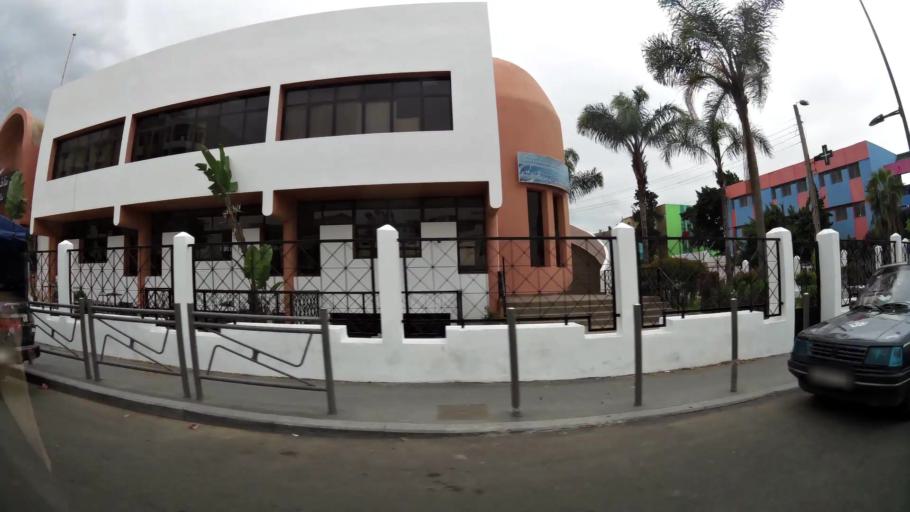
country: MA
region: Grand Casablanca
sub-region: Casablanca
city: Casablanca
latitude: 33.5691
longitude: -7.6173
